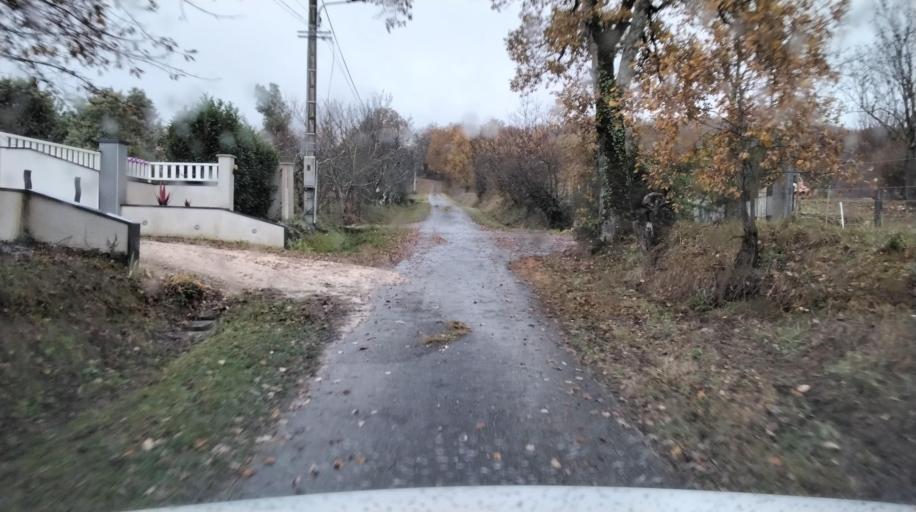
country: FR
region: Midi-Pyrenees
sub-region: Departement de la Haute-Garonne
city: Cazeres
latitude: 43.1644
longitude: 1.1443
